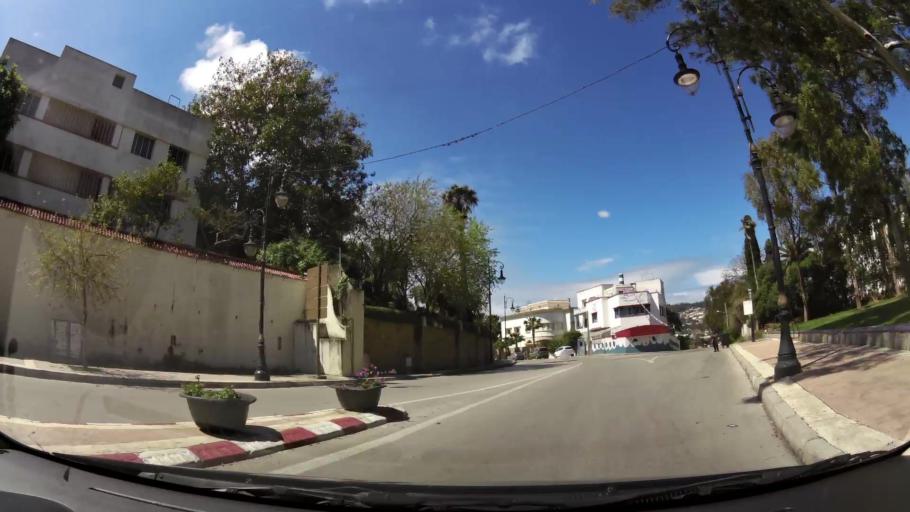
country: MA
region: Tanger-Tetouan
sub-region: Tanger-Assilah
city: Tangier
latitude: 35.7788
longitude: -5.8339
